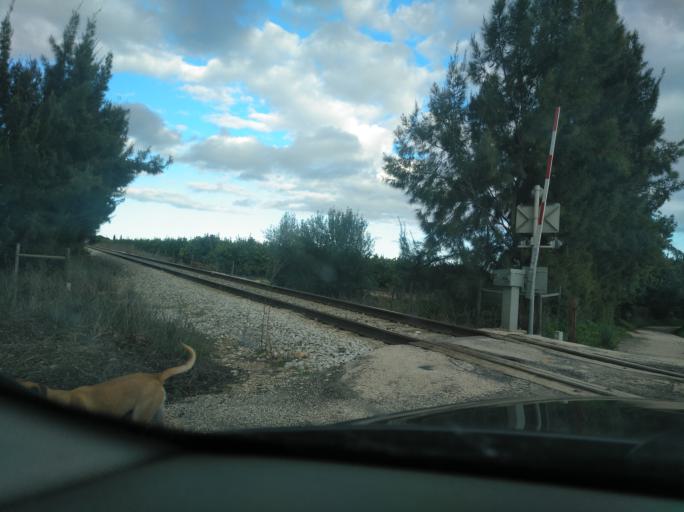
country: PT
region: Faro
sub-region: Tavira
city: Tavira
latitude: 37.1479
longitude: -7.5949
